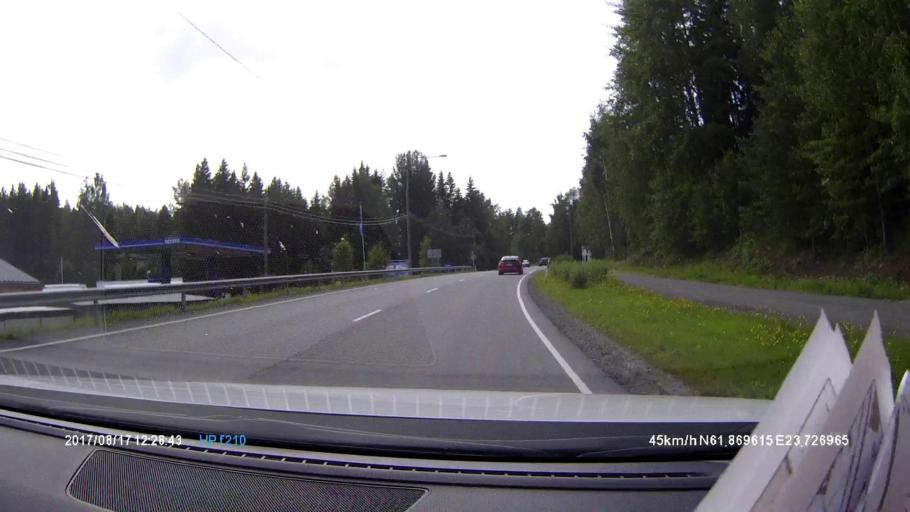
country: FI
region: Pirkanmaa
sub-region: Tampere
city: Kuru
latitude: 61.8693
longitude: 23.7270
